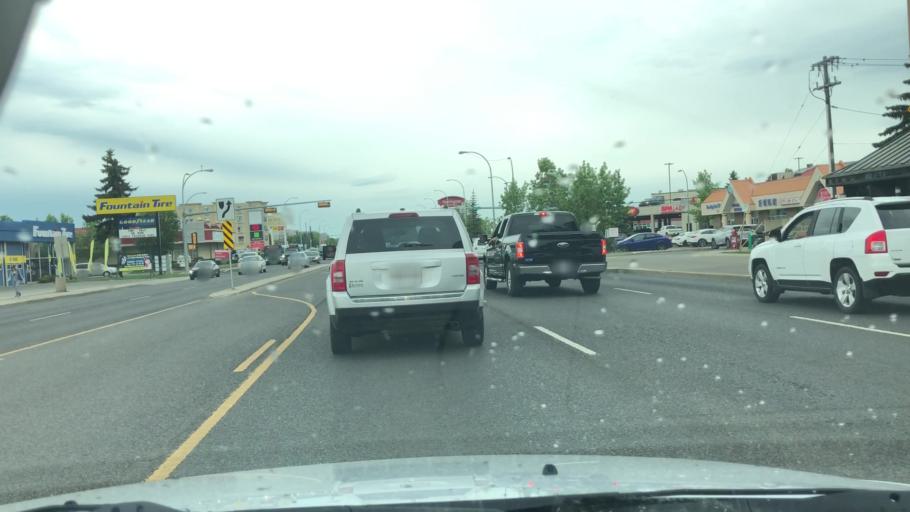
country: CA
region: Alberta
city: Edmonton
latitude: 53.5959
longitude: -113.4919
